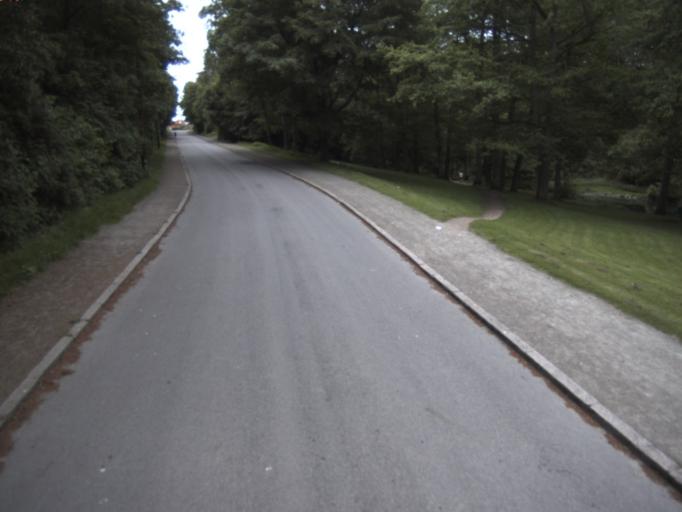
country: SE
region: Skane
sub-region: Helsingborg
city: Helsingborg
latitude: 56.0355
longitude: 12.7287
